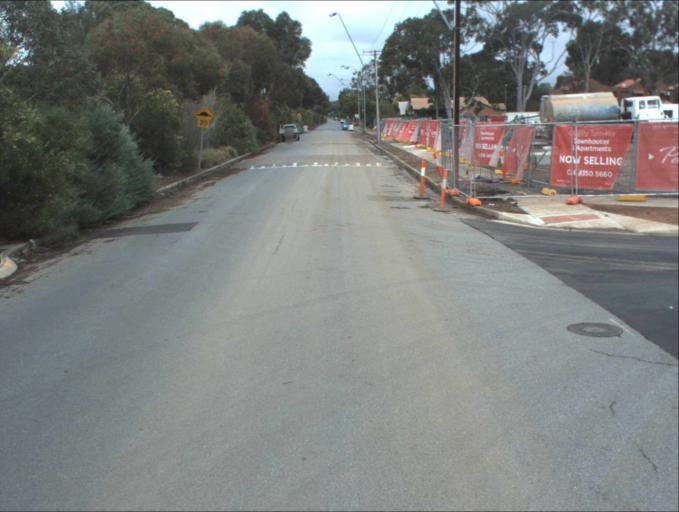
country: AU
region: South Australia
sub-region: Prospect
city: Prospect
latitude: -34.8889
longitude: 138.5834
